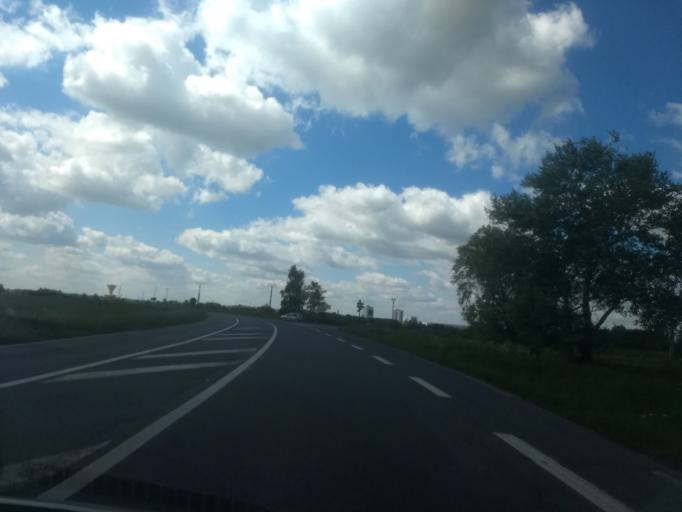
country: FR
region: Nord-Pas-de-Calais
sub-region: Departement du Pas-de-Calais
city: Saint-Laurent-Blangy
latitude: 50.3160
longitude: 2.8058
